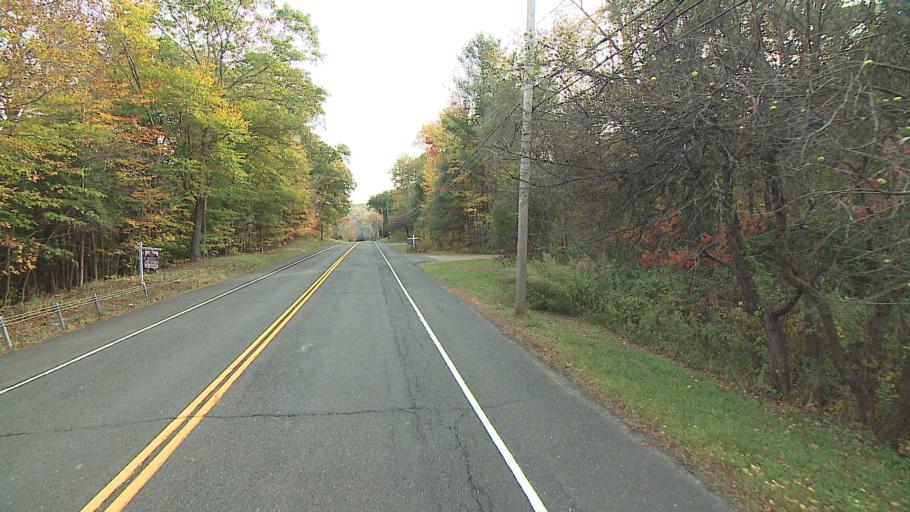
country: US
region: Connecticut
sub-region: Litchfield County
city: Winchester Center
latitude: 41.9502
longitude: -73.1146
